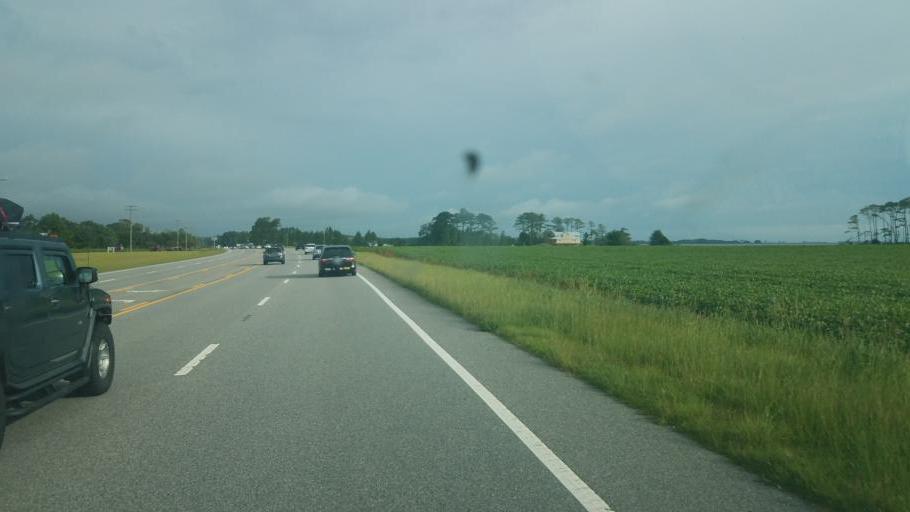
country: US
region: North Carolina
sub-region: Currituck County
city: Currituck
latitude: 36.4005
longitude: -75.9861
